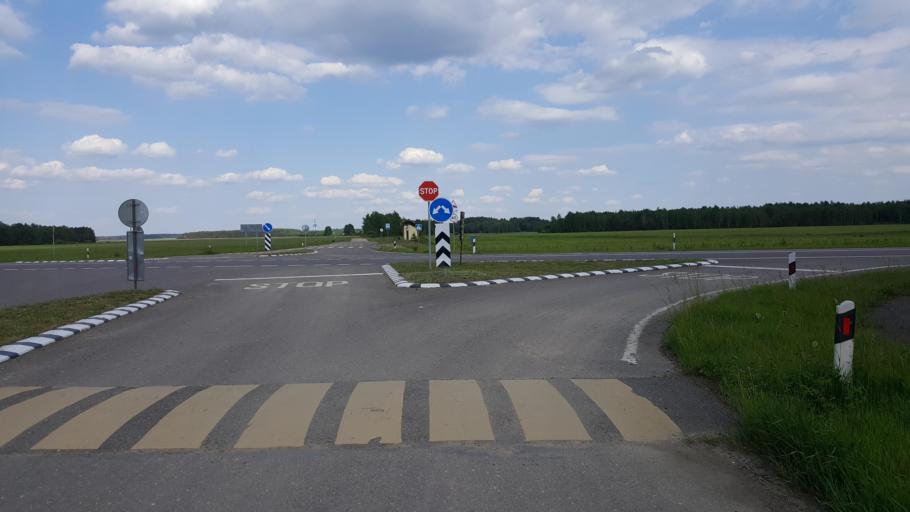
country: BY
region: Brest
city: Zhabinka
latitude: 52.4598
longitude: 24.1408
